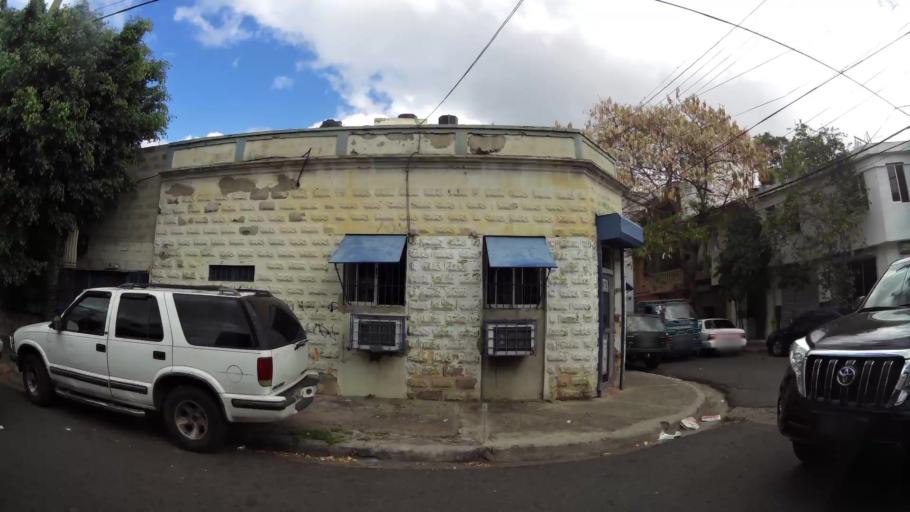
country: DO
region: Nacional
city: San Carlos
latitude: 18.4823
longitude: -69.9005
